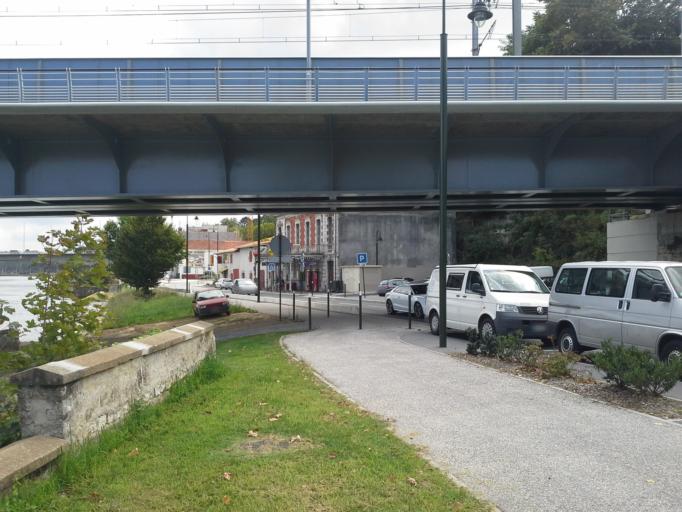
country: FR
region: Aquitaine
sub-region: Departement des Pyrenees-Atlantiques
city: Bayonne
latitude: 43.4885
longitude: -1.4653
